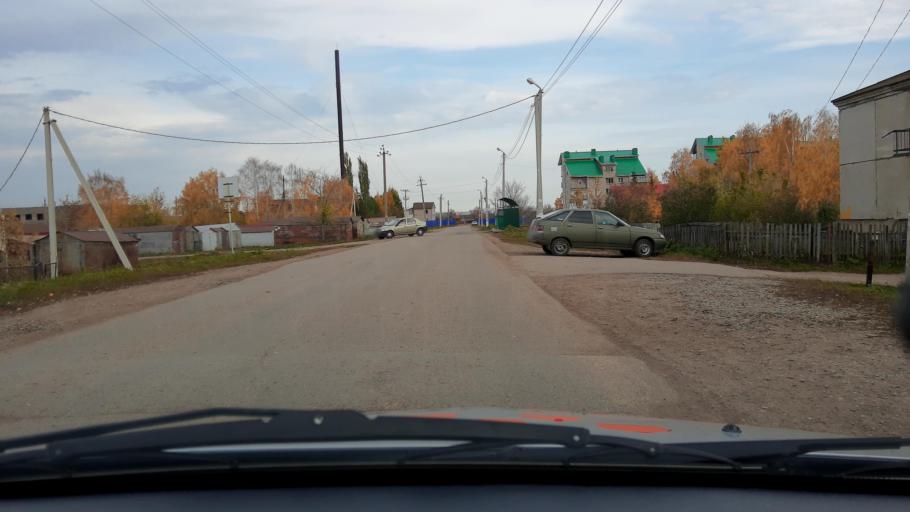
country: RU
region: Bashkortostan
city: Mikhaylovka
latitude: 54.7818
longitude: 55.8379
